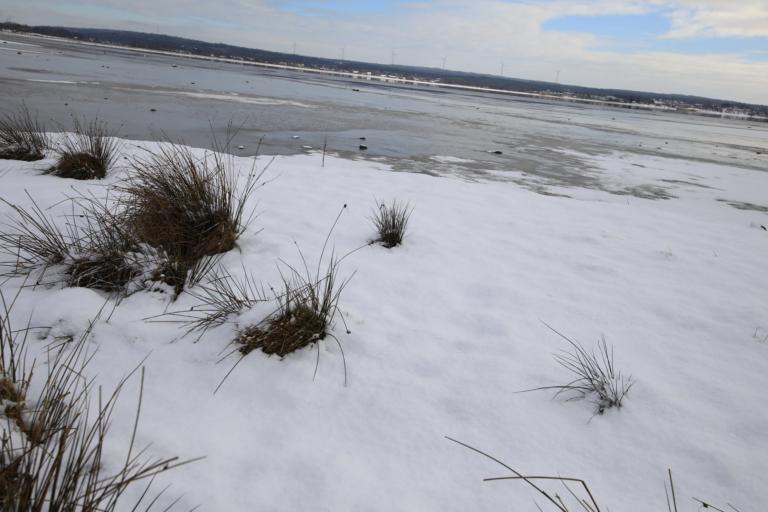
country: SE
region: Halland
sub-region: Kungsbacka Kommun
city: Frillesas
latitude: 57.2221
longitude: 12.1906
